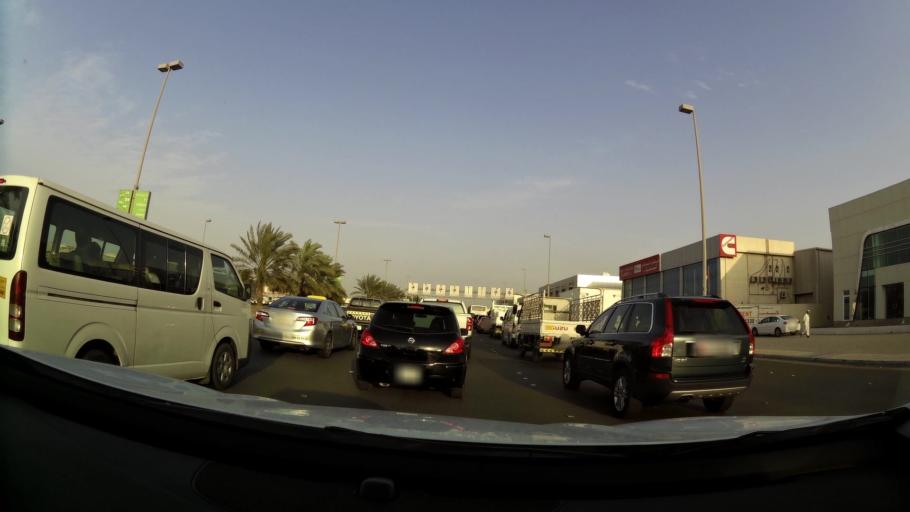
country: AE
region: Abu Dhabi
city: Abu Dhabi
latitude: 24.3730
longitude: 54.5081
